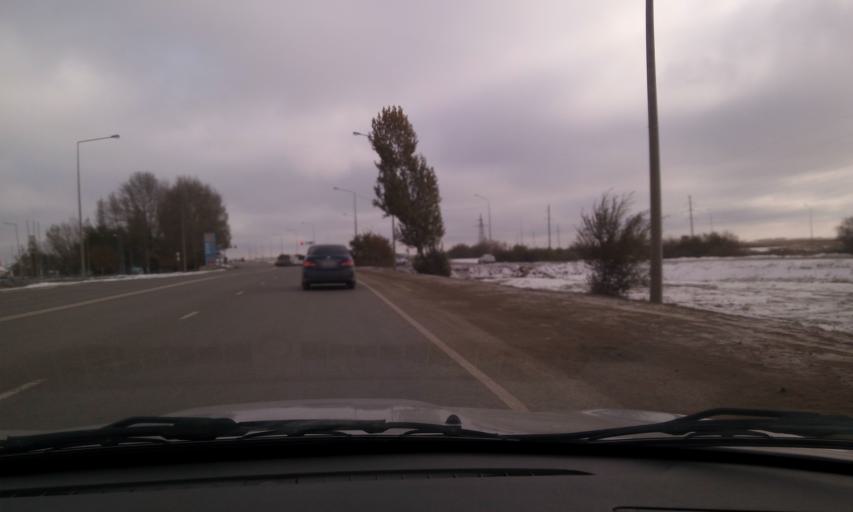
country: KZ
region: Astana Qalasy
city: Astana
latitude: 51.1357
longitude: 71.5419
